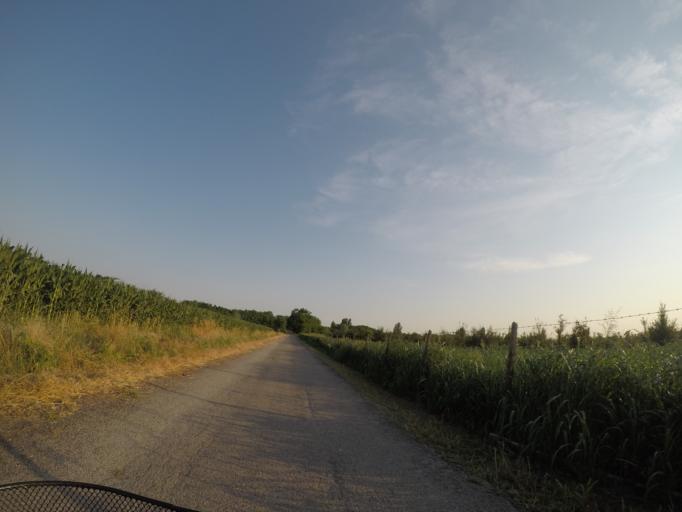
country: IT
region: Veneto
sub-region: Provincia di Rovigo
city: Fratta Polesine
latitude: 45.0115
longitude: 11.6605
